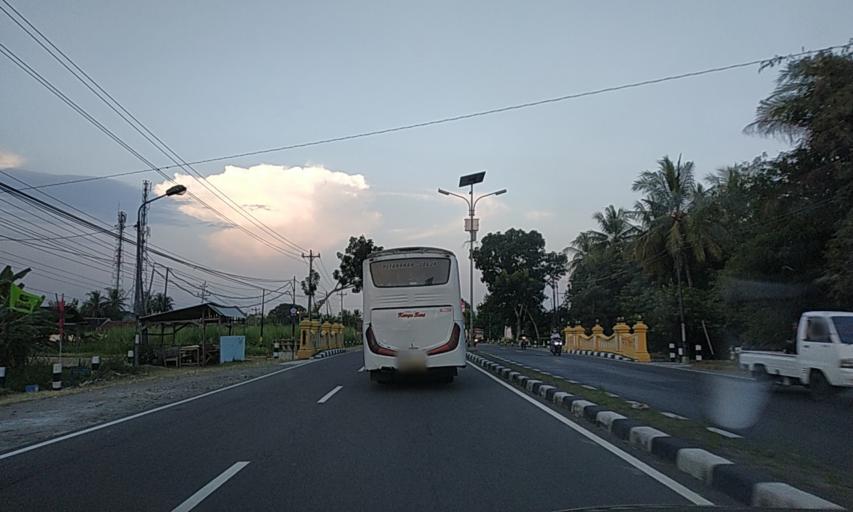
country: ID
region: Daerah Istimewa Yogyakarta
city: Srandakan
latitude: -7.8693
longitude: 110.1469
